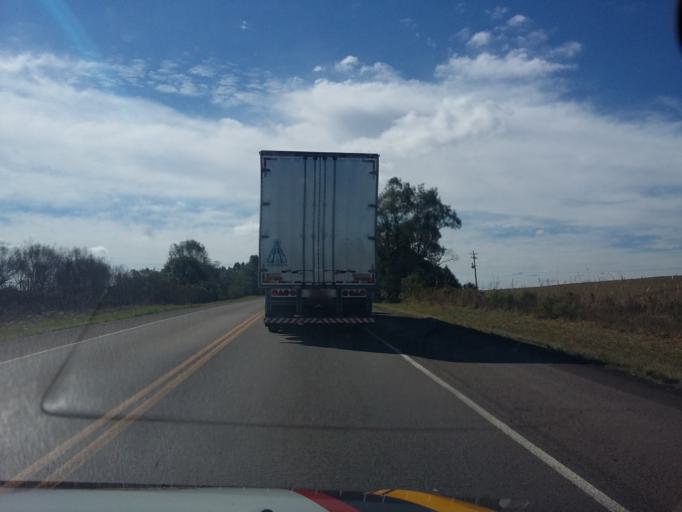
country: BR
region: Rio Grande do Sul
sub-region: Vacaria
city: Vacaria
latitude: -28.6053
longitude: -51.0404
